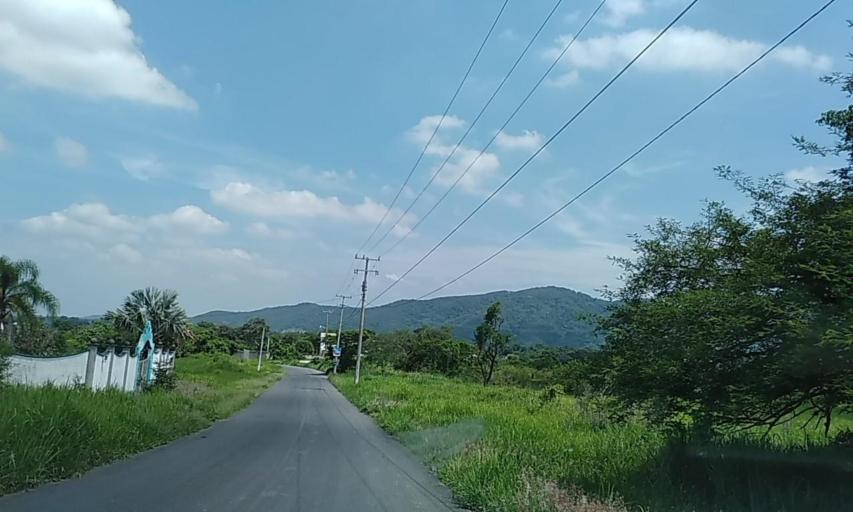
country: MX
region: Veracruz
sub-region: Emiliano Zapata
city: Dos Rios
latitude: 19.4400
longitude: -96.7803
